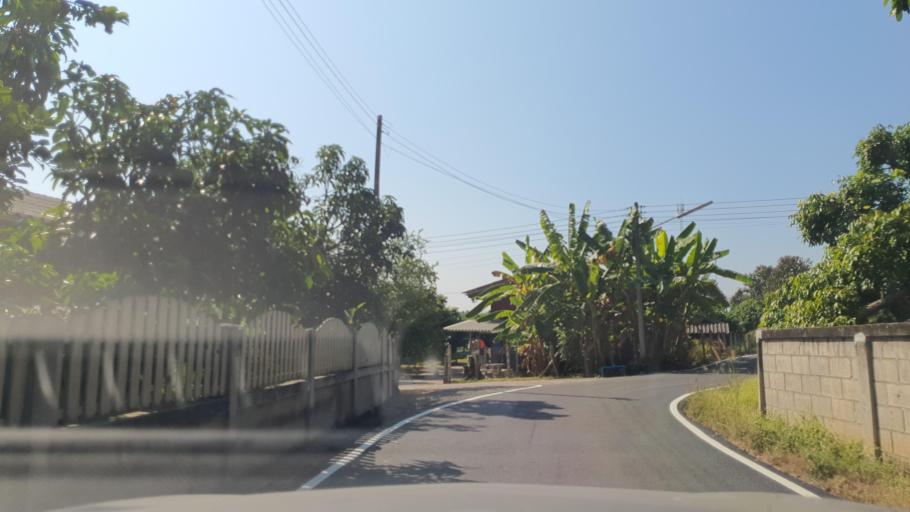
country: TH
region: Lamphun
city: Mae Tha
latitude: 18.5545
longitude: 99.2480
